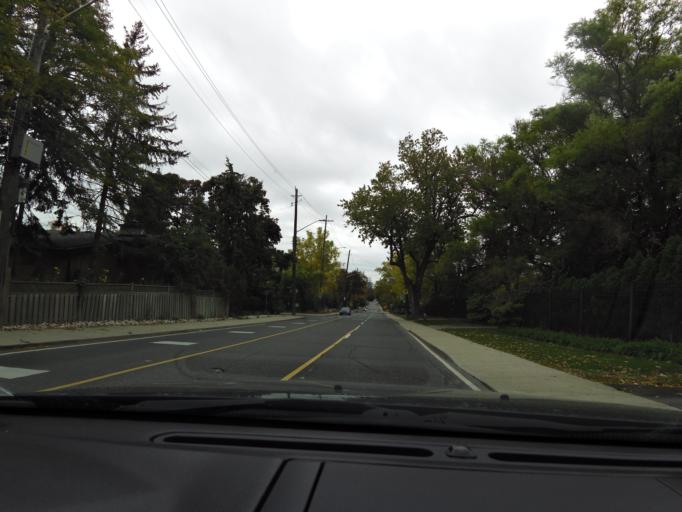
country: CA
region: Ontario
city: Hamilton
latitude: 43.2460
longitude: -79.8842
